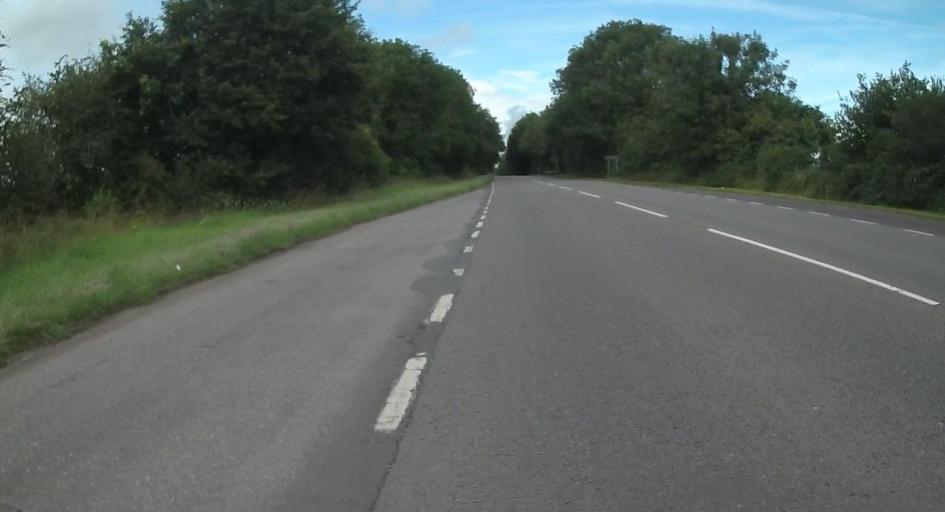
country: GB
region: England
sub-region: Hampshire
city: Overton
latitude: 51.2495
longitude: -1.3348
